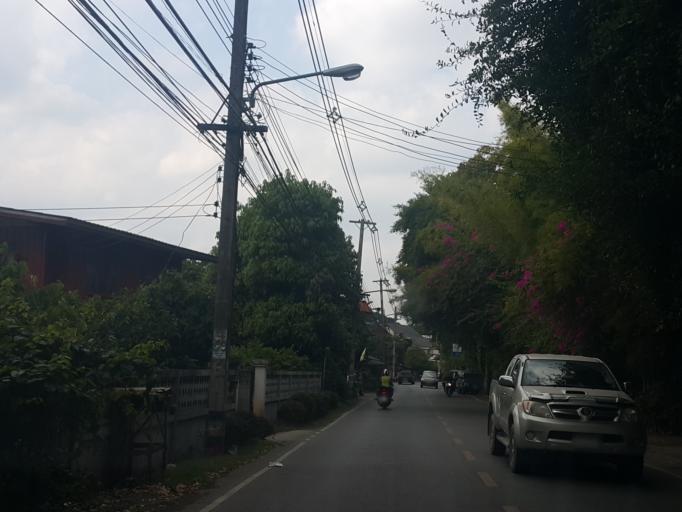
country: TH
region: Chiang Mai
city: Chiang Mai
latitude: 18.8321
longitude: 98.9923
